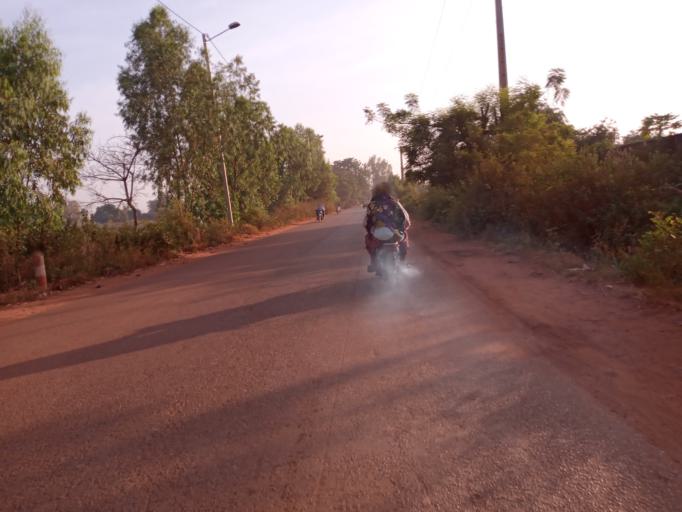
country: ML
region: Bamako
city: Bamako
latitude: 12.6334
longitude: -7.9386
